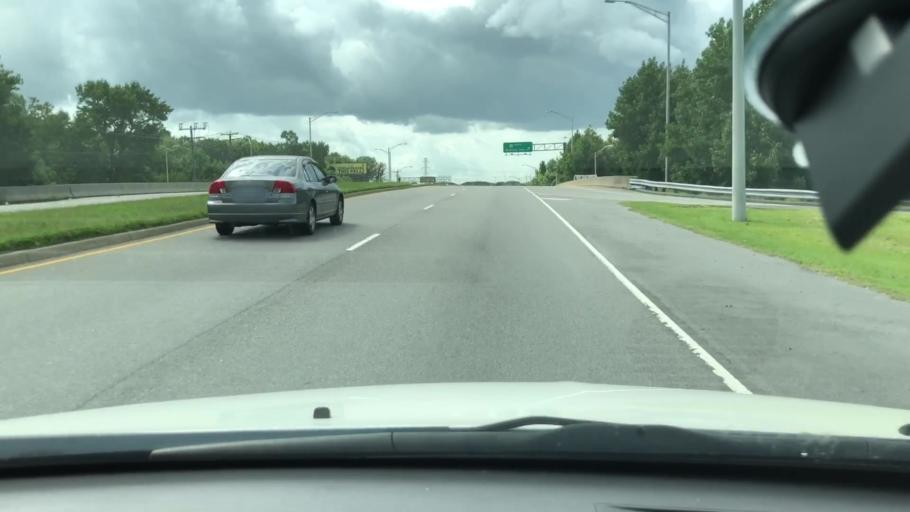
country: US
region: Virginia
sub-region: City of Chesapeake
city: Chesapeake
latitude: 36.7839
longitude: -76.2588
